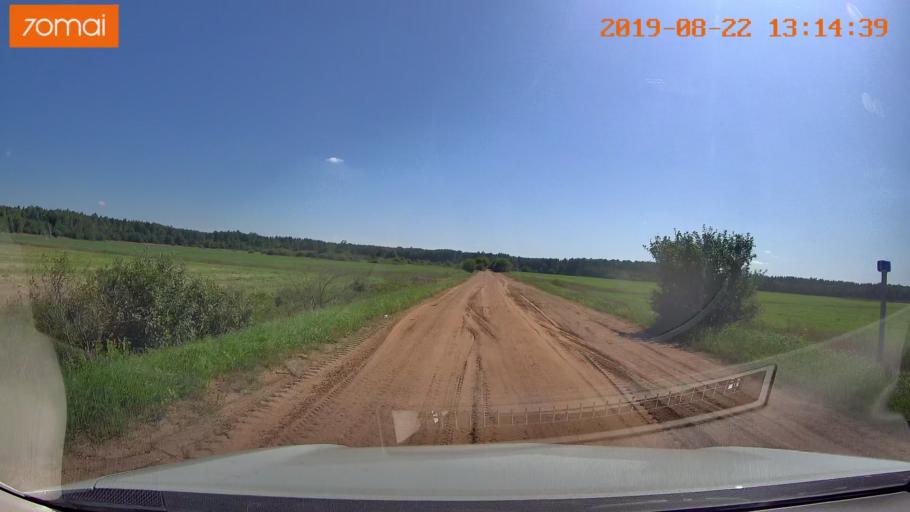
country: BY
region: Minsk
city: Prawdzinski
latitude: 53.2660
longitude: 27.8895
